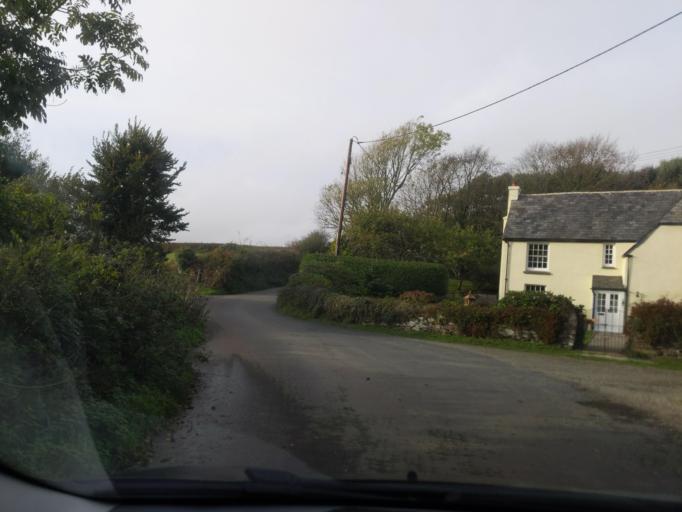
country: GB
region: England
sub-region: Cornwall
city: Looe
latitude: 50.3702
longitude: -4.4156
